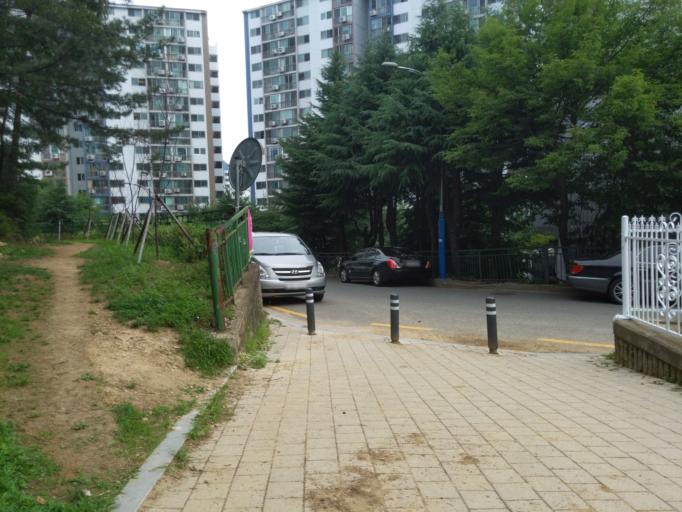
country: KR
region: Daegu
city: Hwawon
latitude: 35.8024
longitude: 128.5343
